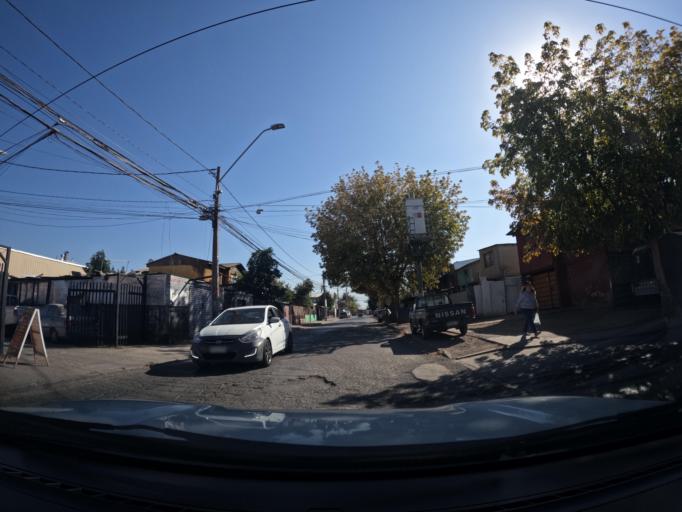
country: CL
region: Santiago Metropolitan
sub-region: Provincia de Santiago
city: Villa Presidente Frei, Nunoa, Santiago, Chile
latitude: -33.4788
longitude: -70.5729
